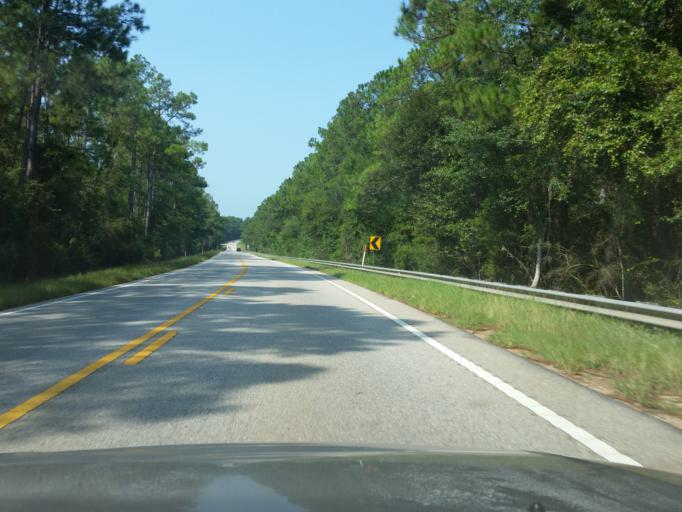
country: US
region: Florida
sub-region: Escambia County
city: Cantonment
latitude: 30.5210
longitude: -87.4587
